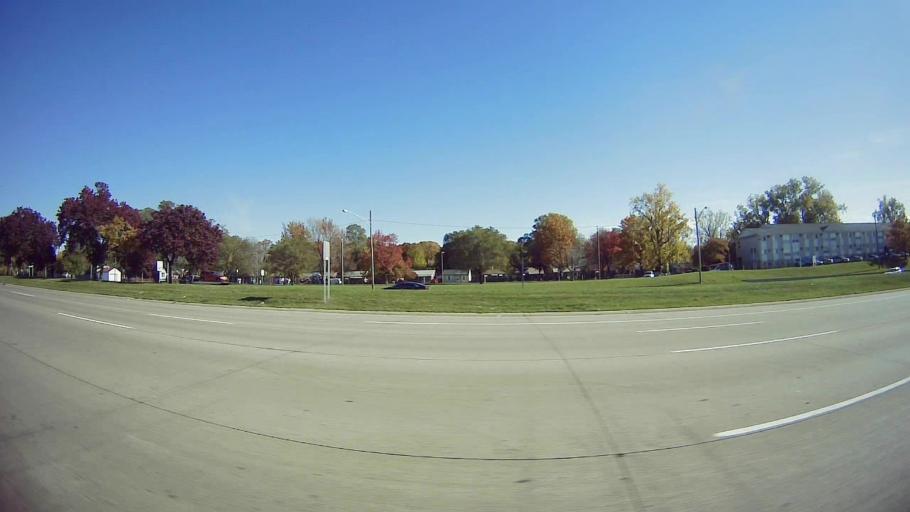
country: US
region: Michigan
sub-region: Wayne County
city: Redford
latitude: 42.3797
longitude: -83.2758
